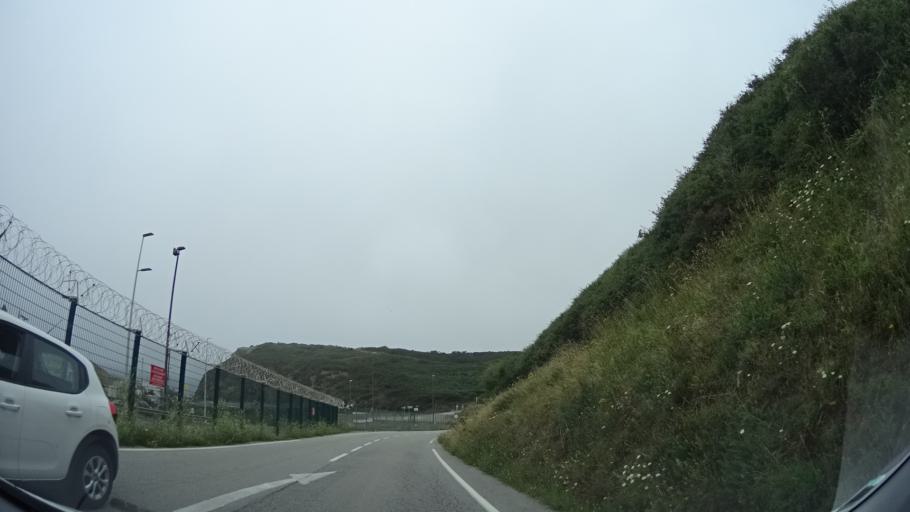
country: FR
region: Lower Normandy
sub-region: Departement de la Manche
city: Flamanville
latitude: 49.5419
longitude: -1.8739
